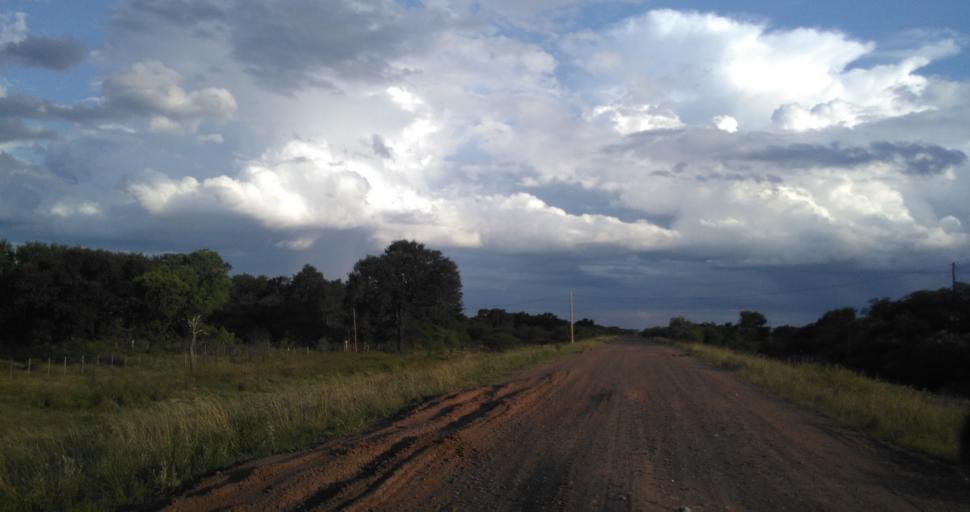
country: AR
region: Chaco
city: Resistencia
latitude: -27.4152
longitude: -58.9404
